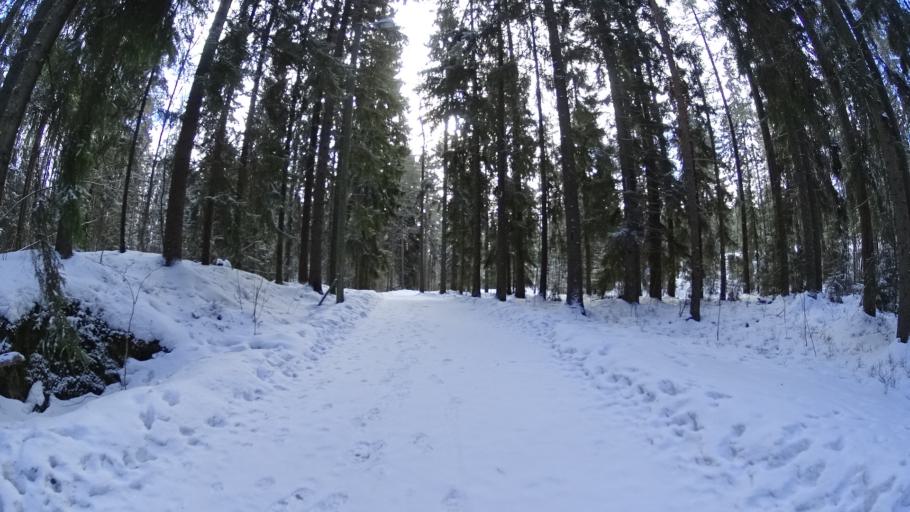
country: FI
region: Uusimaa
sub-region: Helsinki
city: Teekkarikylae
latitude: 60.2640
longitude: 24.8899
